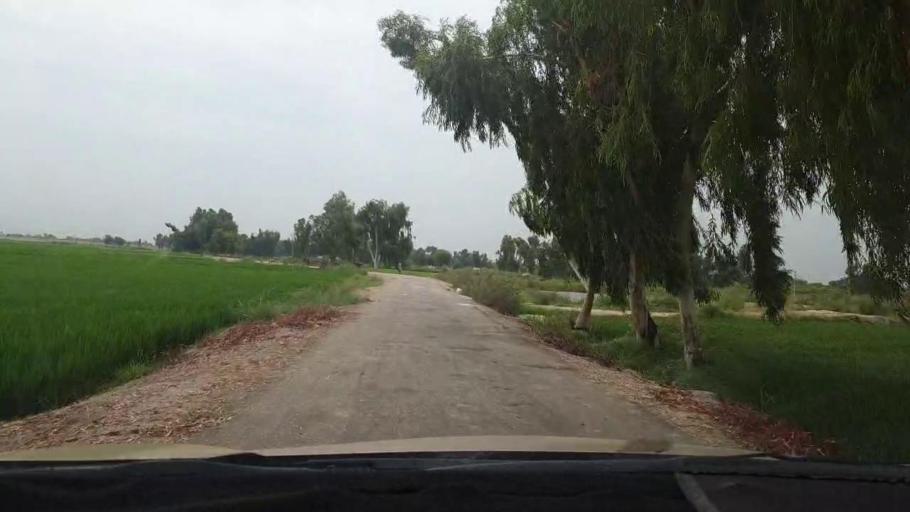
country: PK
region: Sindh
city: Naudero
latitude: 27.6237
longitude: 68.3248
